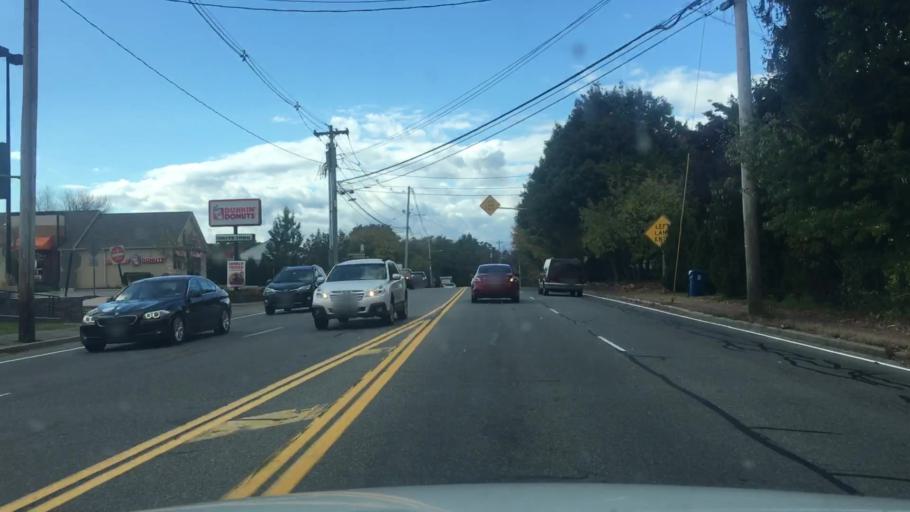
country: US
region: Maine
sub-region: Cumberland County
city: South Portland Gardens
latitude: 43.6590
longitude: -70.2976
